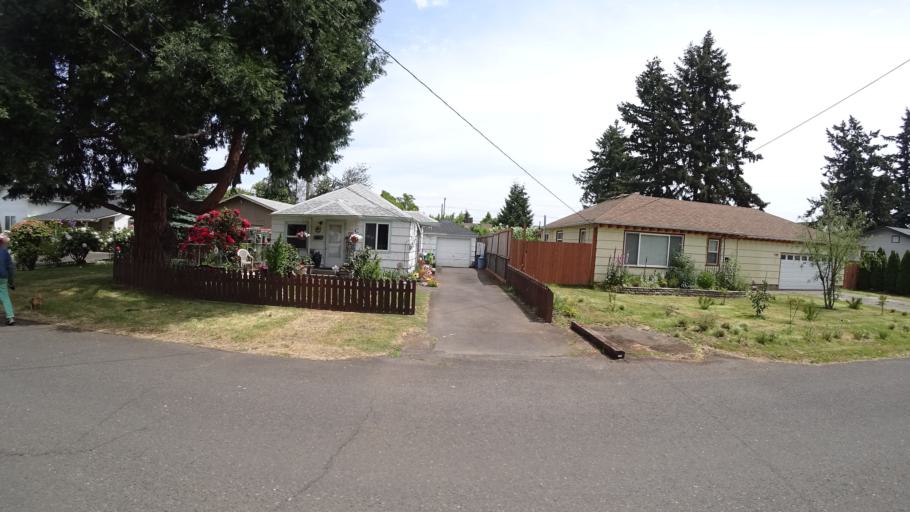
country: US
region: Oregon
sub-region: Multnomah County
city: Lents
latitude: 45.4701
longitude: -122.5904
